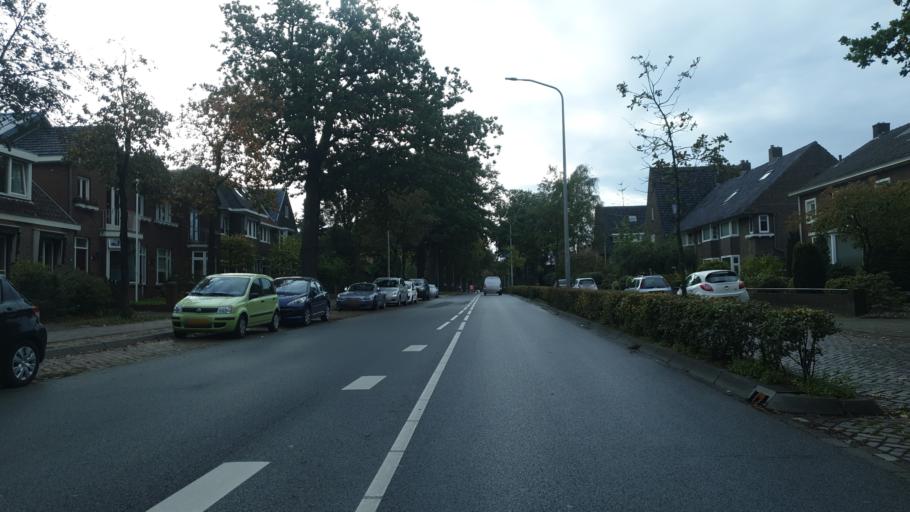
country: NL
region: Gelderland
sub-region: Gemeente Nijmegen
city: Nijmegen
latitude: 51.8292
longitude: 5.8751
